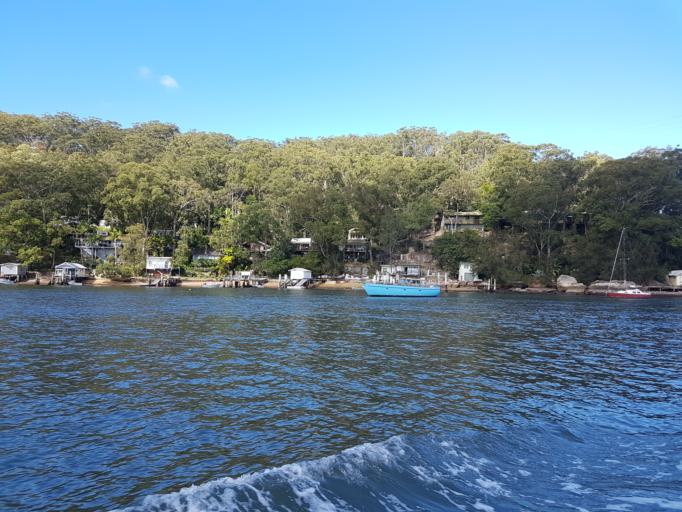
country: AU
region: New South Wales
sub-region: Gosford Shire
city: Umina
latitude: -33.5391
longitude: 151.2342
